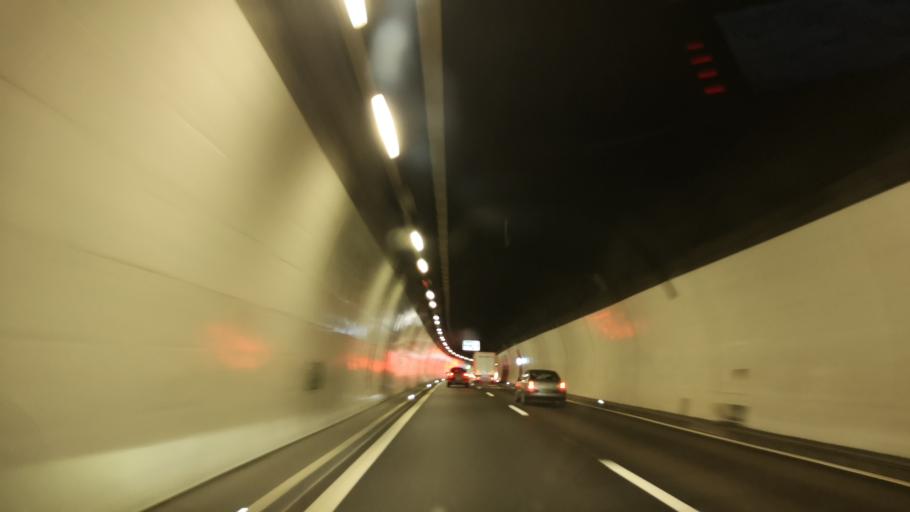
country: CH
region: Ticino
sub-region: Lugano District
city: Montagnola
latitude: 45.9902
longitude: 8.9266
